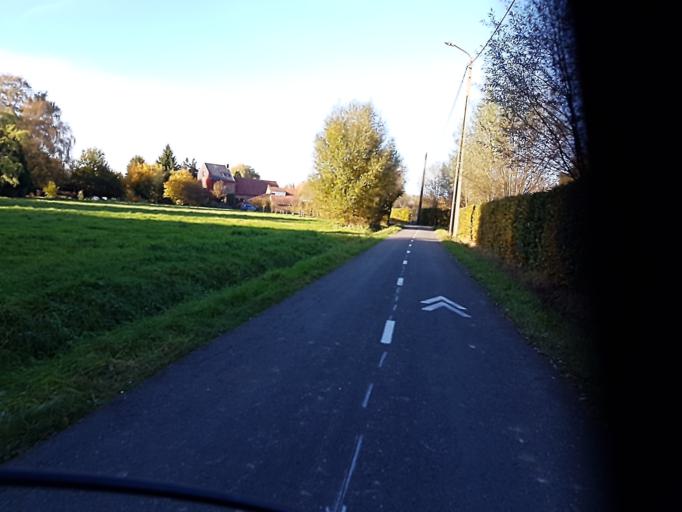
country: BE
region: Flanders
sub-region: Provincie Antwerpen
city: Bonheiden
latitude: 51.0435
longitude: 4.5396
